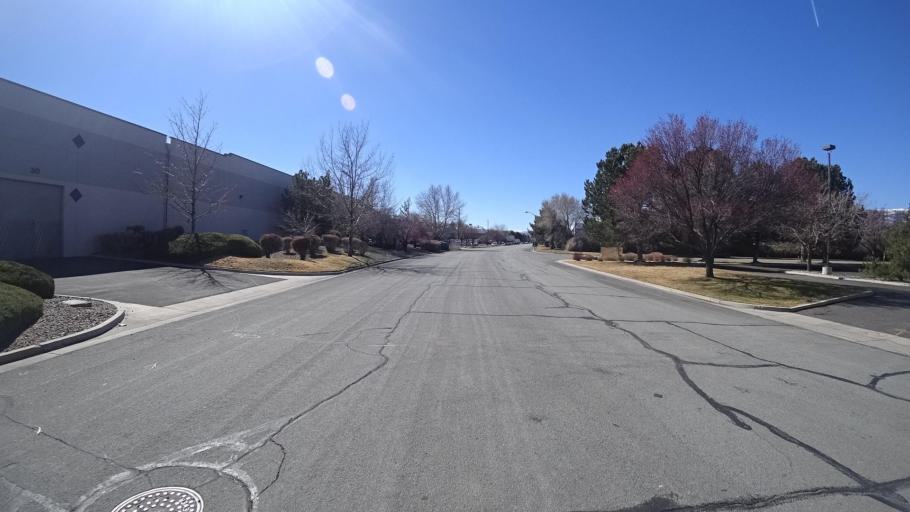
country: US
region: Nevada
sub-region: Washoe County
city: Sparks
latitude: 39.4863
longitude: -119.7626
